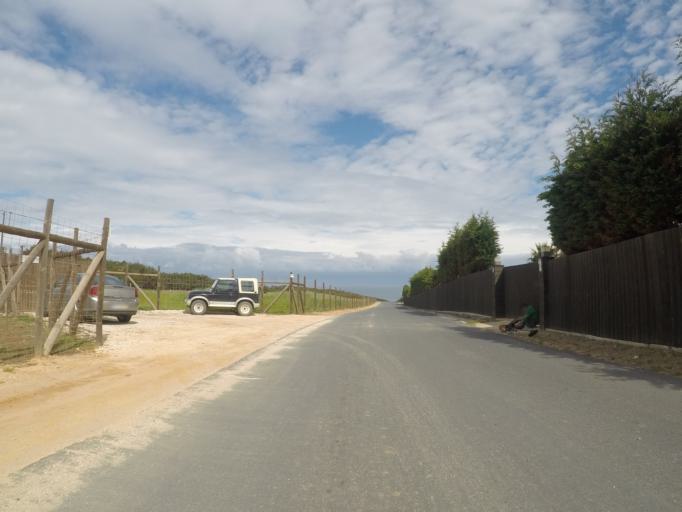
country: PT
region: Beja
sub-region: Odemira
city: Sao Teotonio
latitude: 37.4962
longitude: -8.7893
